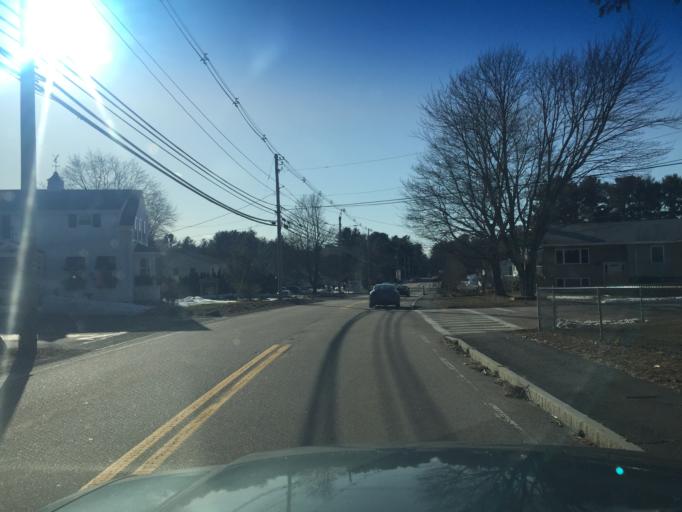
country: US
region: Massachusetts
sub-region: Norfolk County
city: Bellingham
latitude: 42.0865
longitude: -71.4824
